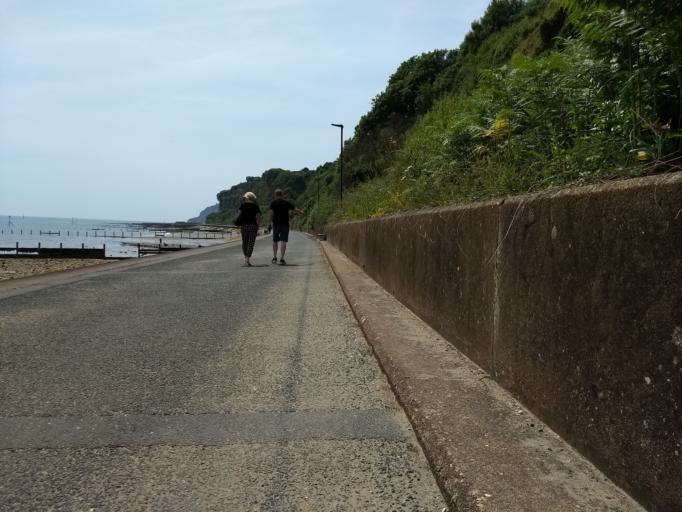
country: GB
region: England
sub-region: Isle of Wight
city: Sandown
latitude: 50.6415
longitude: -1.1681
